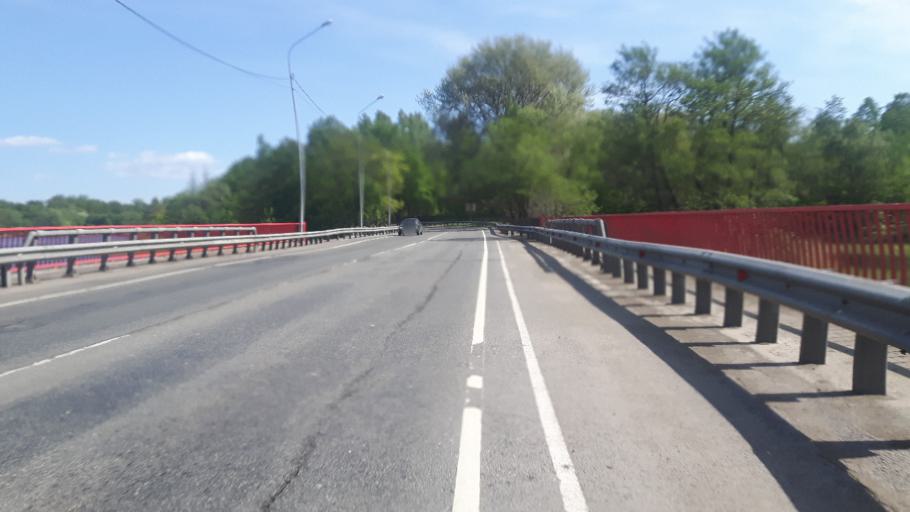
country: RU
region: Leningrad
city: Vyborg
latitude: 60.7253
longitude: 28.7079
